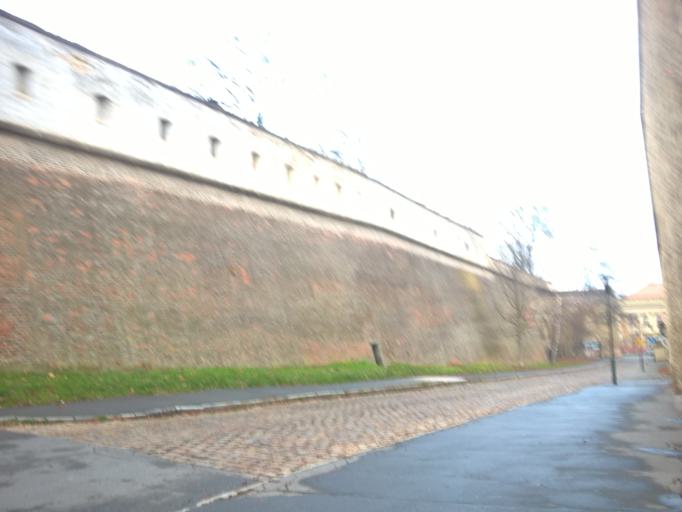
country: CZ
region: Praha
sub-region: Praha 1
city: Mala Strana
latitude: 50.0856
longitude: 14.3874
